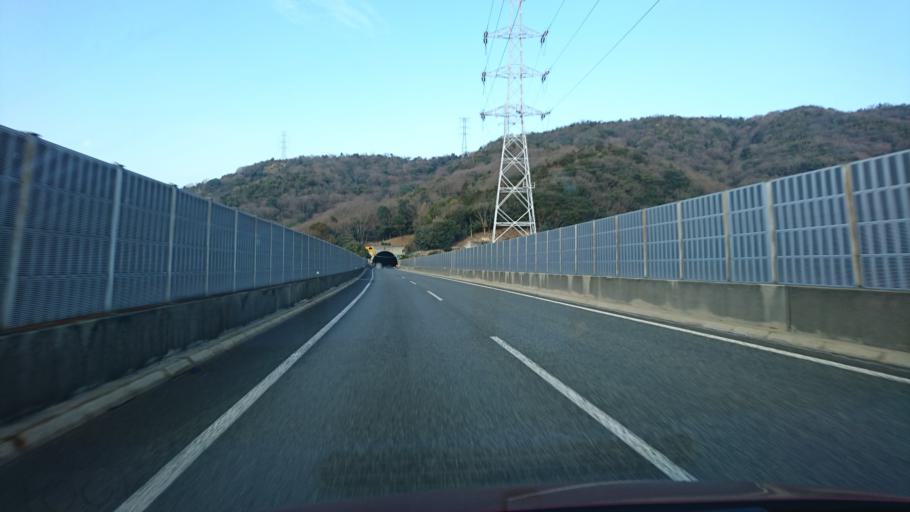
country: JP
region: Hyogo
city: Himeji
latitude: 34.8602
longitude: 134.7210
